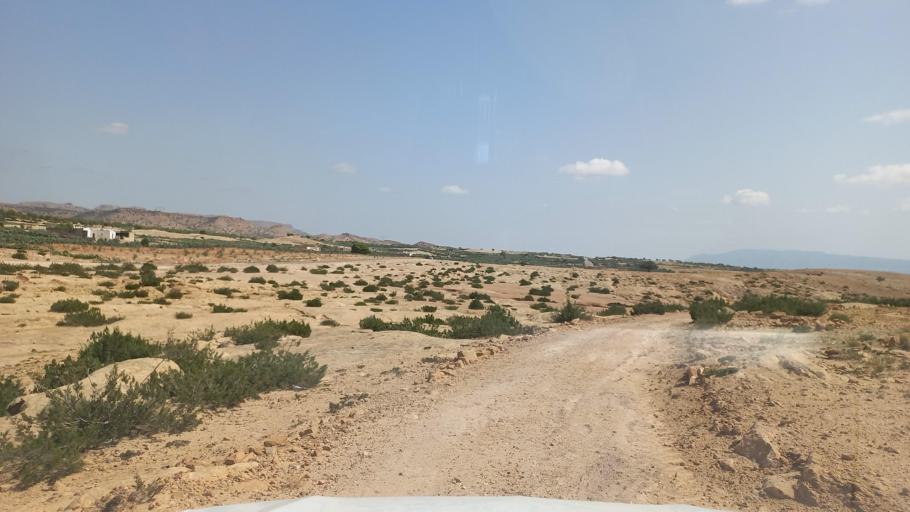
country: TN
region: Al Qasrayn
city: Sbiba
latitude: 35.3979
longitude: 8.9611
